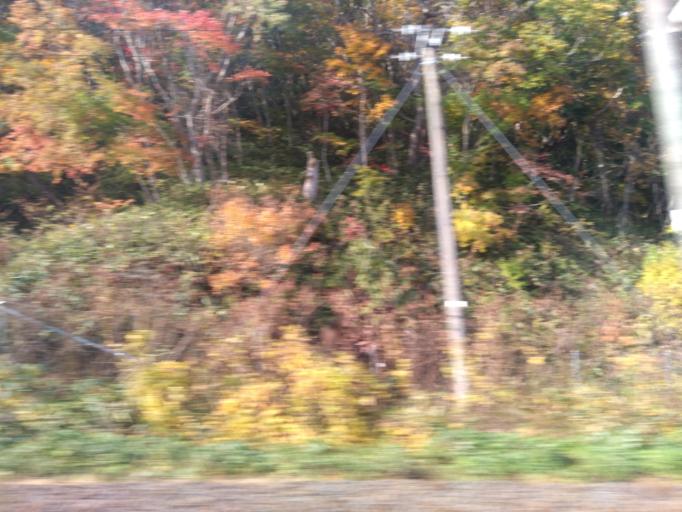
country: JP
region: Hokkaido
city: Shiraoi
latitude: 42.5652
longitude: 141.3772
